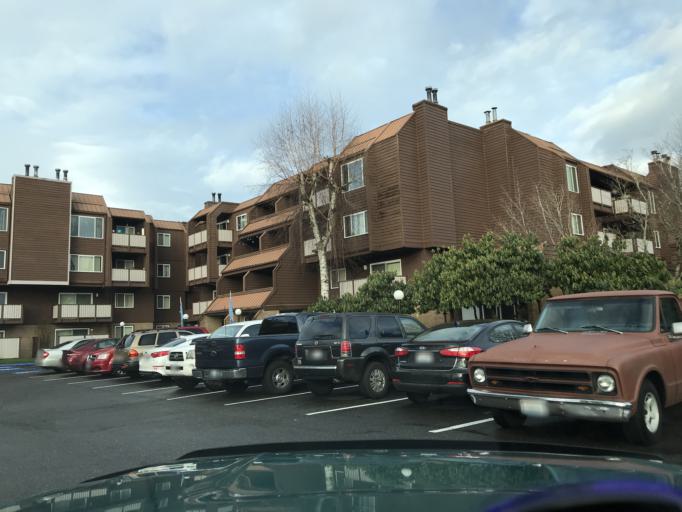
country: US
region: Washington
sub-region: Pierce County
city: Lakewood
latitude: 47.1815
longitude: -122.5436
